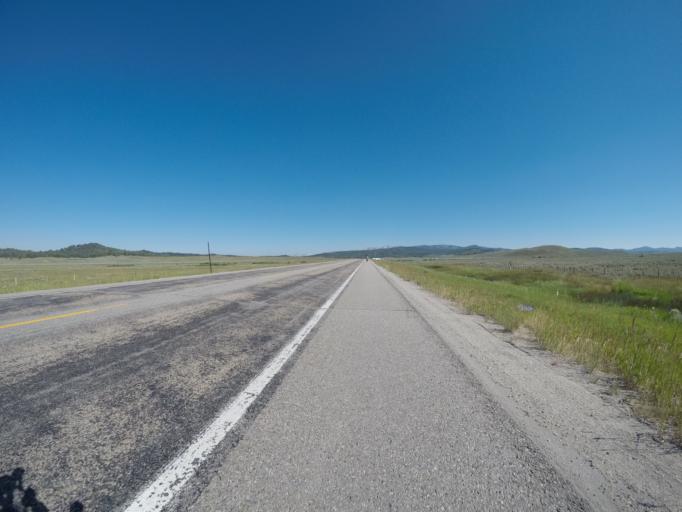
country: US
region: Wyoming
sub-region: Sublette County
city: Pinedale
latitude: 43.1081
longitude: -110.1726
